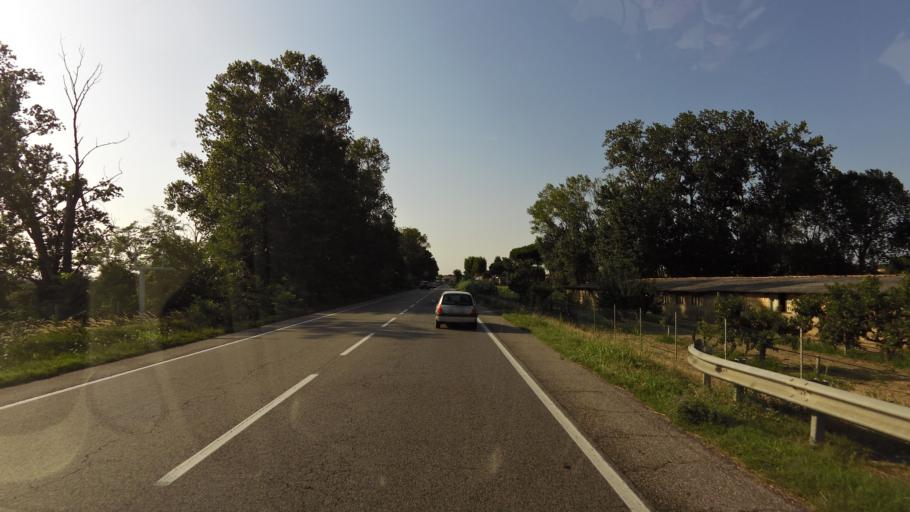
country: IT
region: Emilia-Romagna
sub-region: Provincia di Ravenna
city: Cervia
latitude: 44.2467
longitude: 12.3495
